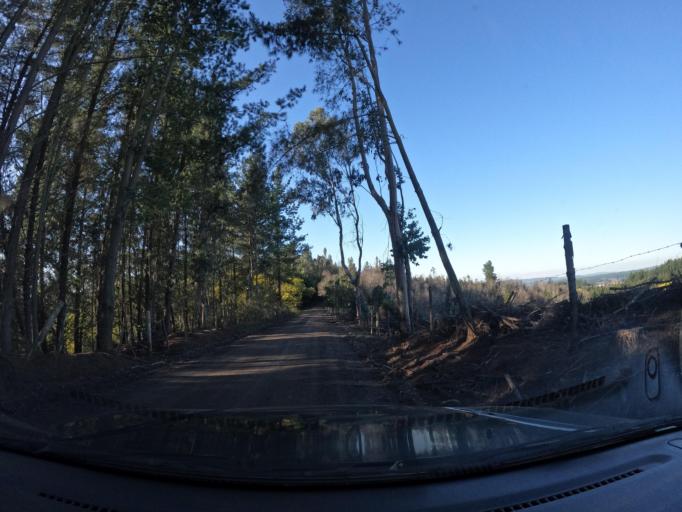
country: CL
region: Biobio
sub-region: Provincia de Concepcion
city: Chiguayante
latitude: -37.0134
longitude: -72.8613
